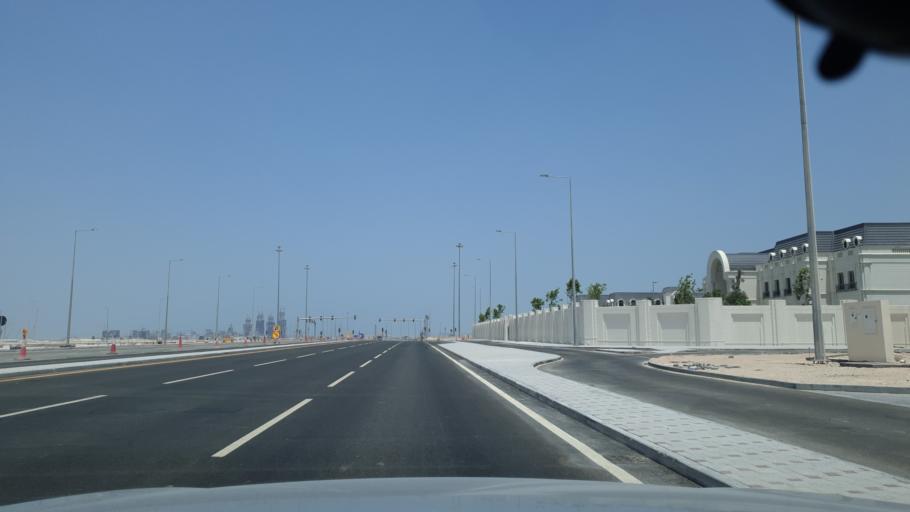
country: QA
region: Baladiyat Umm Salal
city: Umm Salal Muhammad
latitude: 25.3924
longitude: 51.4706
